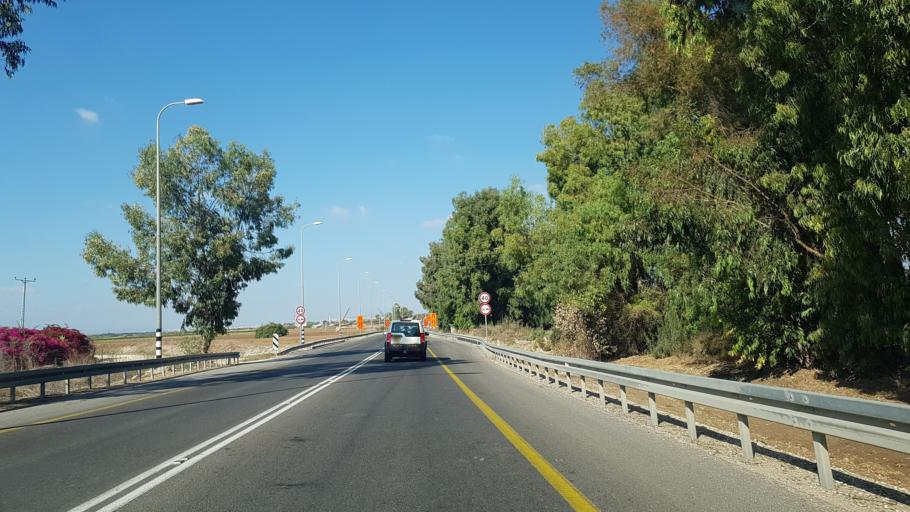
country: PS
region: West Bank
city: Tulkarm
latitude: 32.3308
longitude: 35.0041
